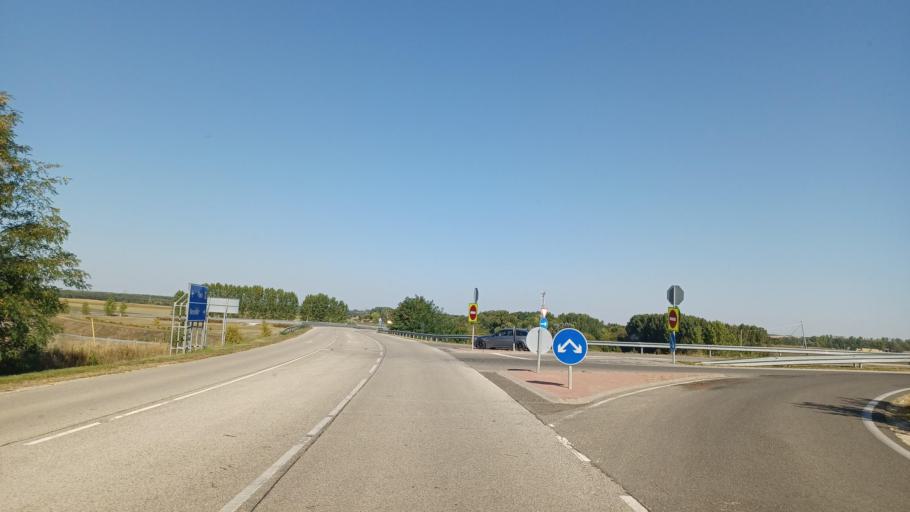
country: HU
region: Tolna
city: Paks
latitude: 46.6710
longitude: 18.8171
